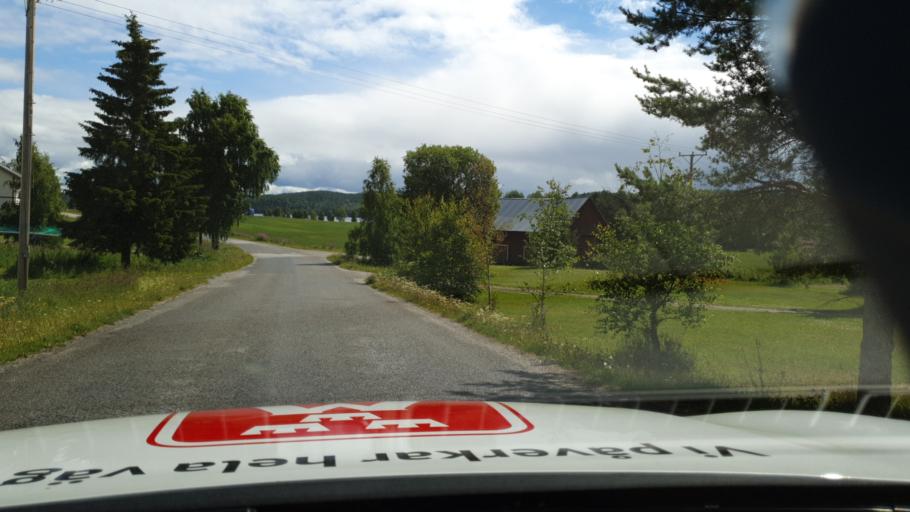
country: SE
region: Jaemtland
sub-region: OEstersunds Kommun
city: Brunflo
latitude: 62.9627
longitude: 15.1232
